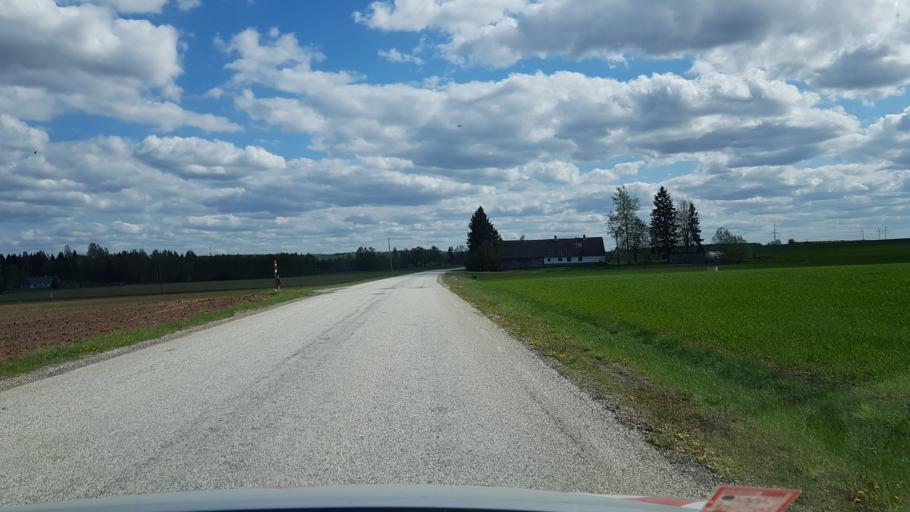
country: EE
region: Tartu
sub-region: UElenurme vald
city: Ulenurme
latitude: 58.2842
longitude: 26.9020
